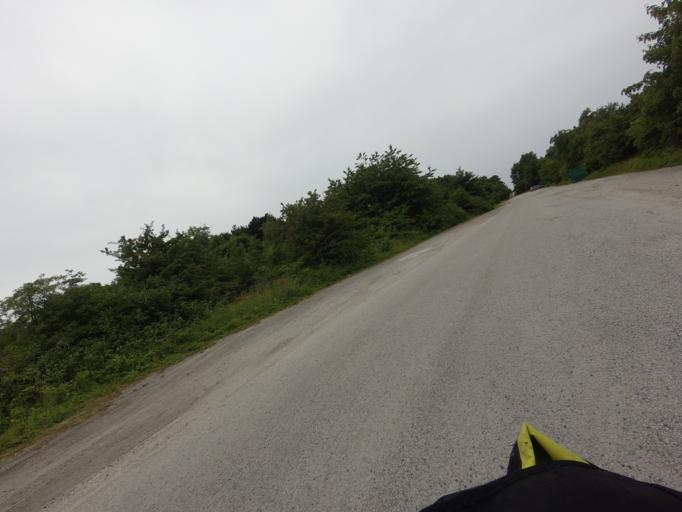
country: SE
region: Skane
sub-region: Malmo
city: Bunkeflostrand
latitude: 55.5238
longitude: 12.8997
